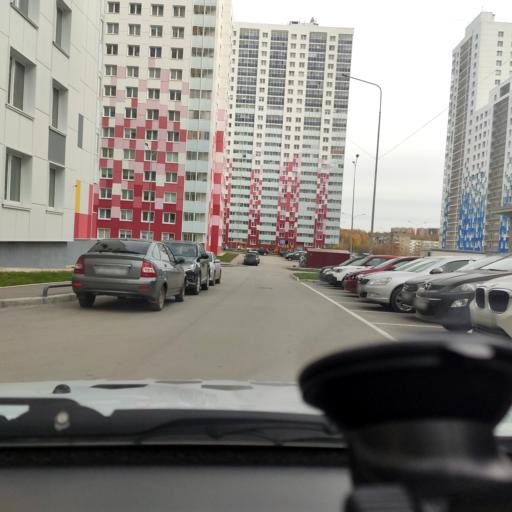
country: RU
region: Perm
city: Perm
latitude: 57.9906
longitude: 56.2656
